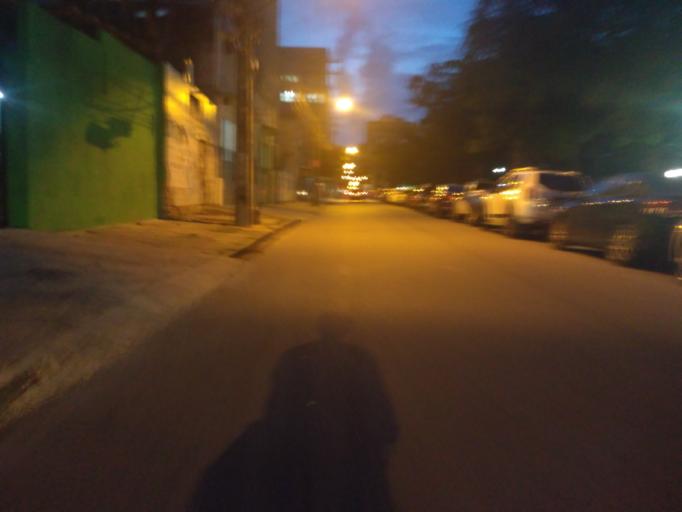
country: BR
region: Pernambuco
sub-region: Recife
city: Recife
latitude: -8.0568
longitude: -34.8799
